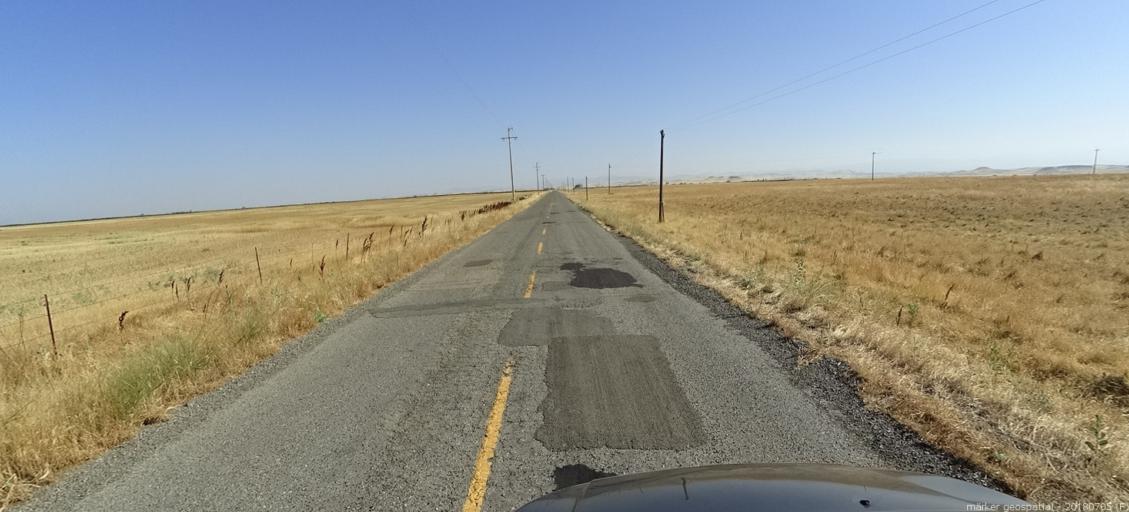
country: US
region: California
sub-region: Madera County
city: Madera Acres
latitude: 37.1396
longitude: -120.0747
